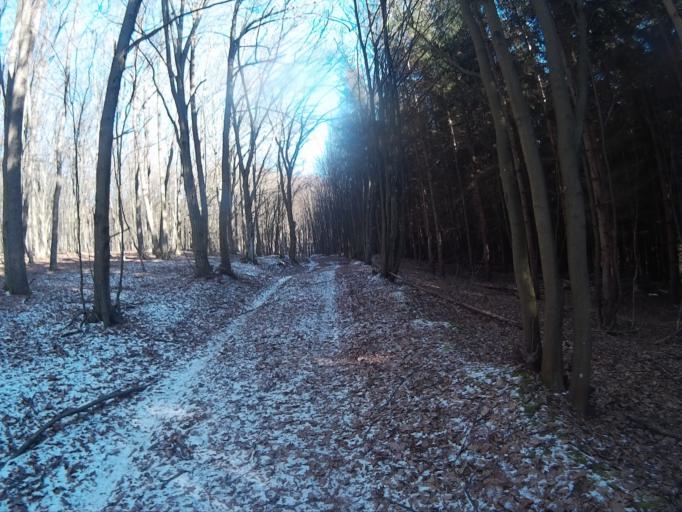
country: HU
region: Borsod-Abauj-Zemplen
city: Rudabanya
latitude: 48.5003
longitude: 20.5952
